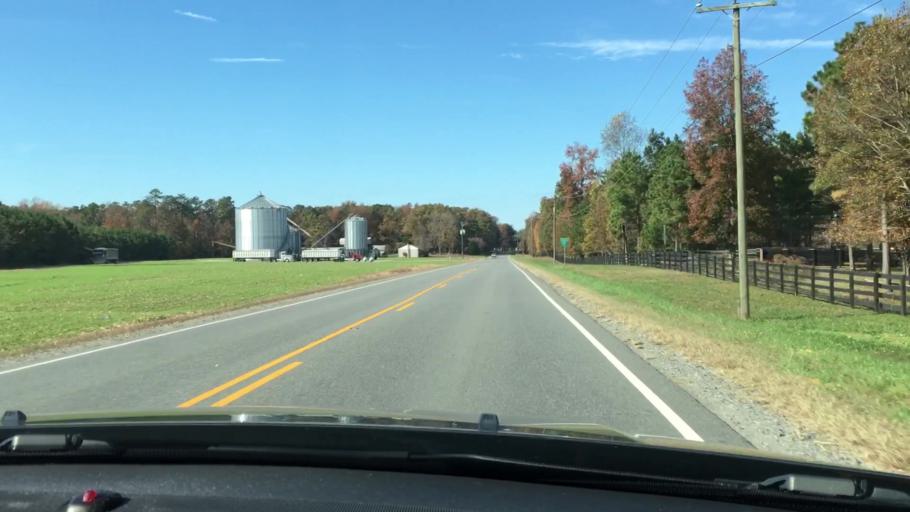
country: US
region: Virginia
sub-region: King and Queen County
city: King and Queen Court House
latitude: 37.5938
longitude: -76.9004
